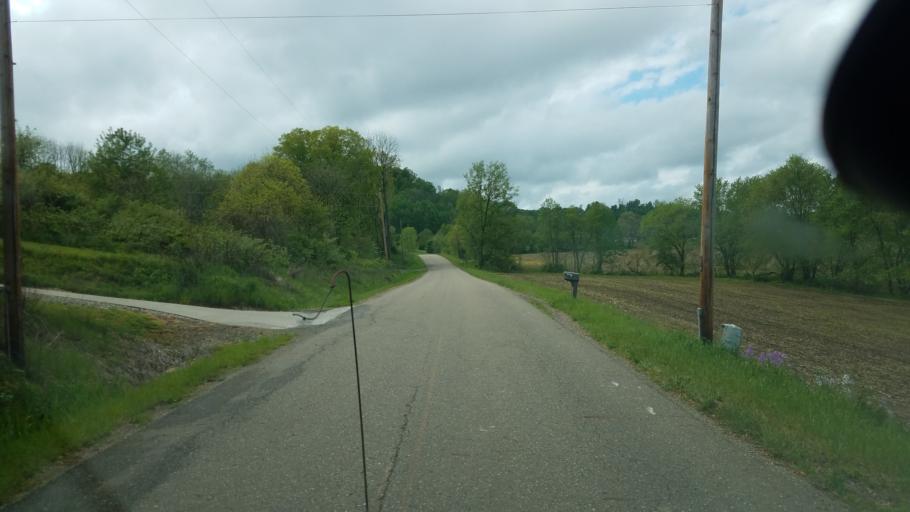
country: US
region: Ohio
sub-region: Tuscarawas County
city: Dover
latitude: 40.5819
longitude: -81.4001
